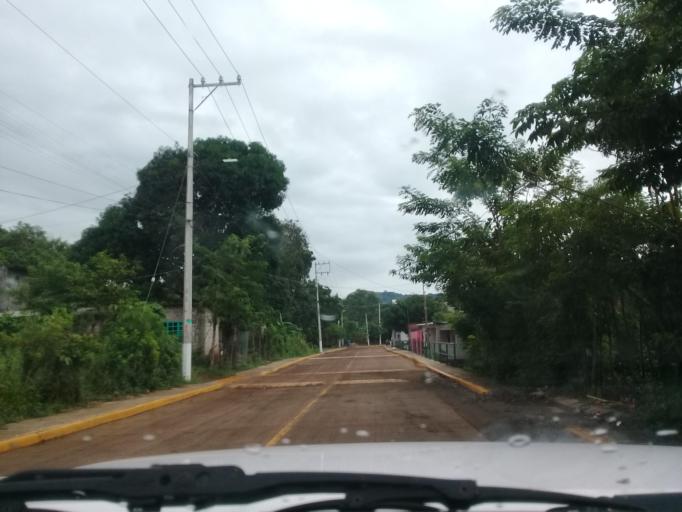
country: MX
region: Veracruz
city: San Andres Tuxtla
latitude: 18.4348
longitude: -95.2102
